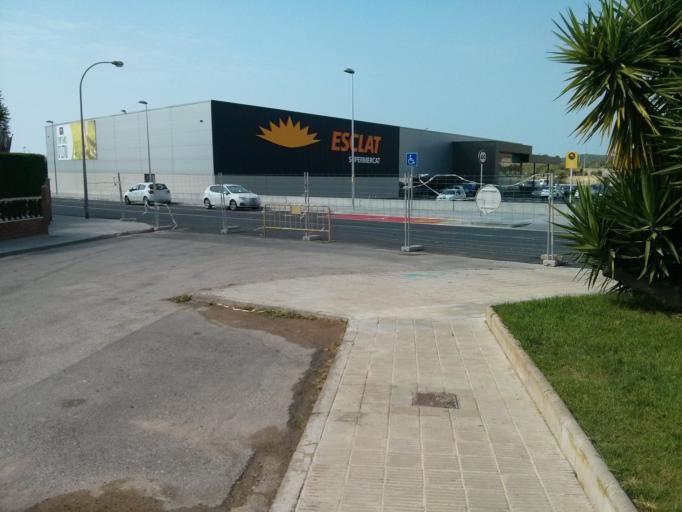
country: ES
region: Catalonia
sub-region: Provincia de Tarragona
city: El Vendrell
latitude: 41.2151
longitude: 1.5298
